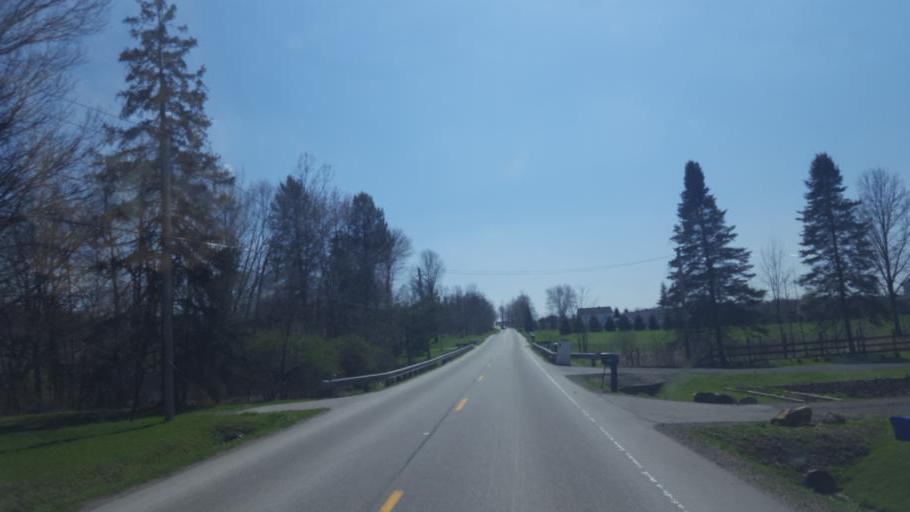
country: US
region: Ohio
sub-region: Geauga County
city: Middlefield
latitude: 41.4175
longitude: -81.1077
